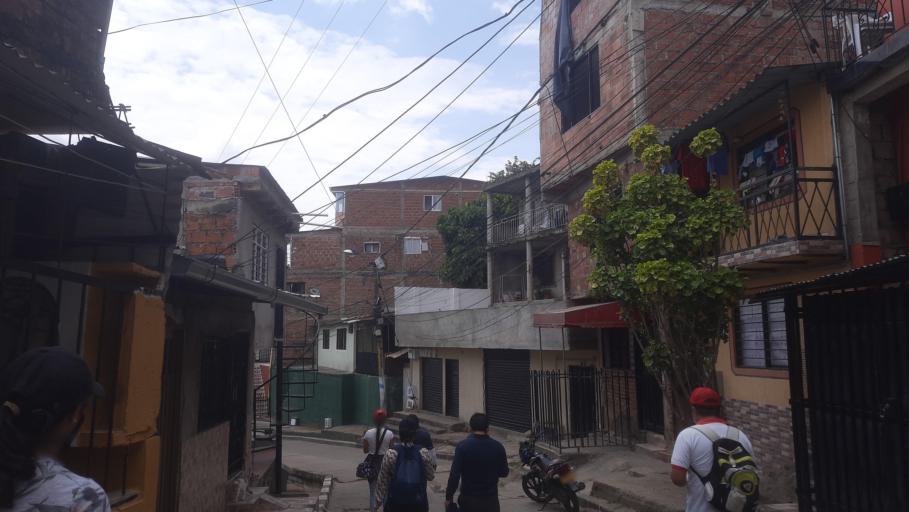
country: CO
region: Valle del Cauca
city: Cali
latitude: 3.3728
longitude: -76.5542
